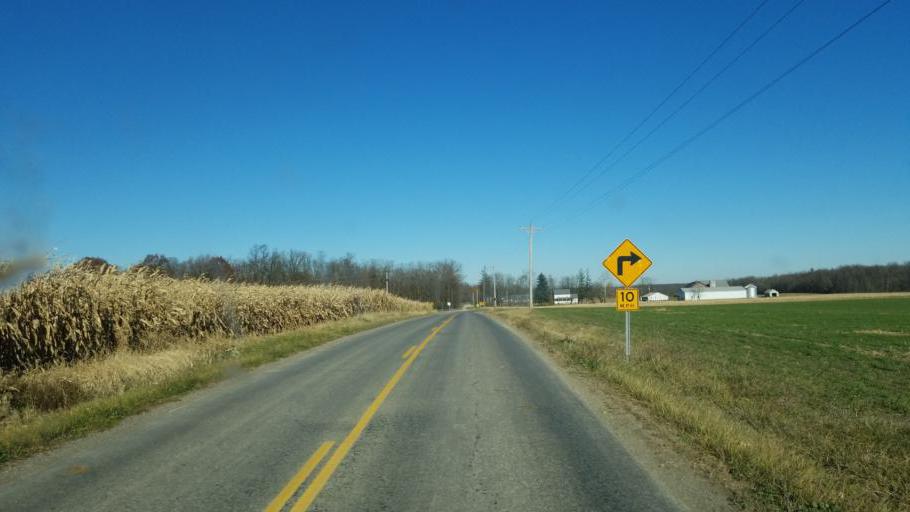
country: US
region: Ohio
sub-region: Ashland County
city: Ashland
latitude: 40.9221
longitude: -82.3877
